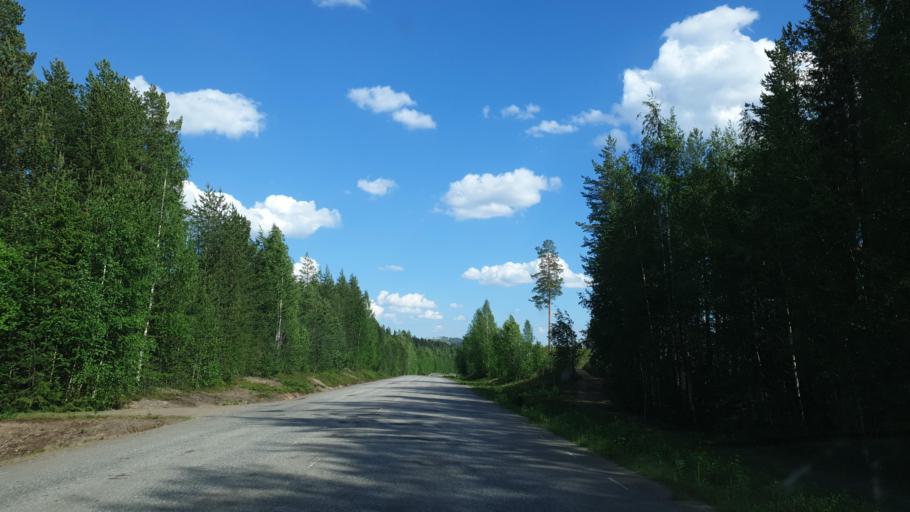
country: SE
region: Norrbotten
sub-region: Alvsbyns Kommun
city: AElvsbyn
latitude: 65.8342
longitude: 20.5287
